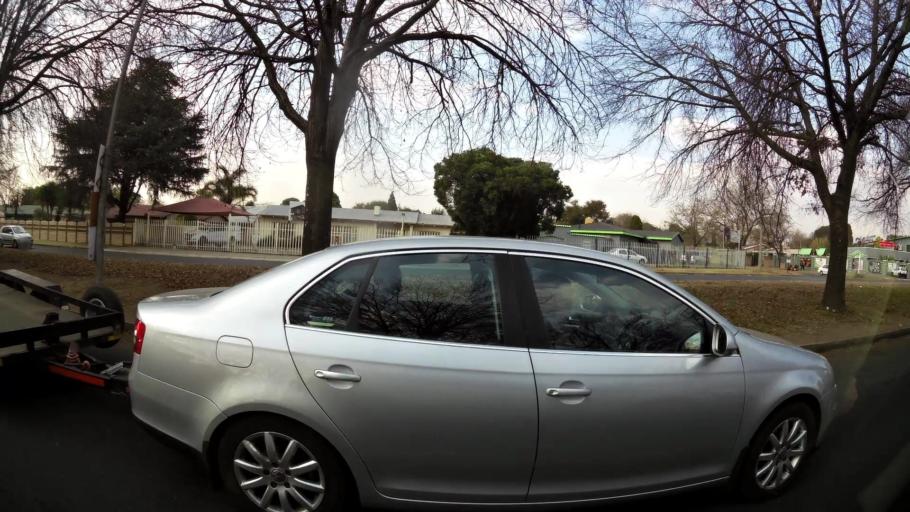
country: ZA
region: Gauteng
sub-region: Ekurhuleni Metropolitan Municipality
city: Benoni
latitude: -26.1490
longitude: 28.2998
